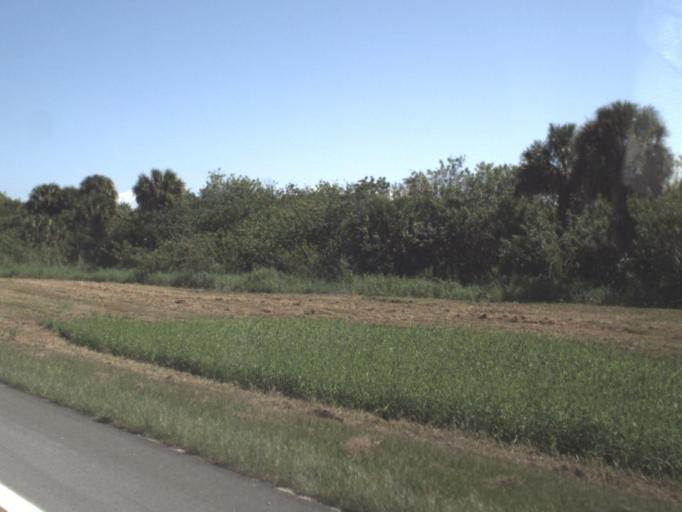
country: US
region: Florida
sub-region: Glades County
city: Moore Haven
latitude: 26.9897
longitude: -81.0906
